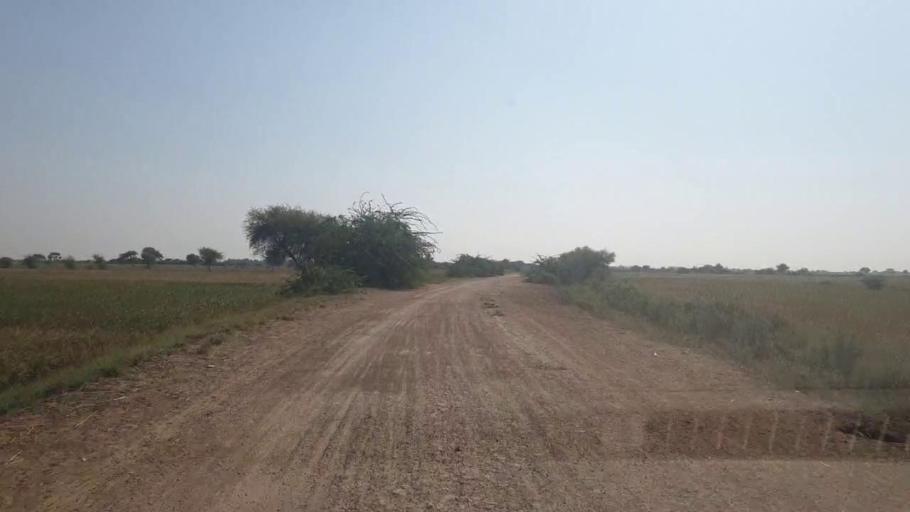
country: PK
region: Sindh
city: Badin
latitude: 24.5607
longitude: 68.8461
